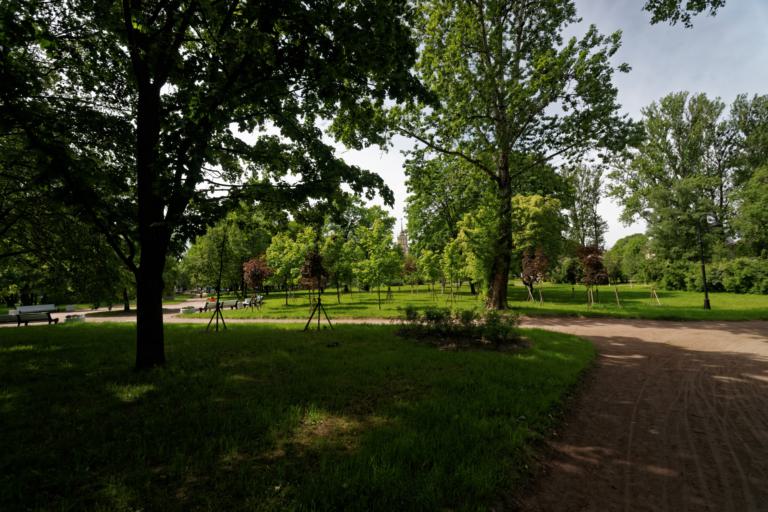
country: RU
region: St.-Petersburg
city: Kupchino
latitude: 59.8657
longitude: 30.3277
